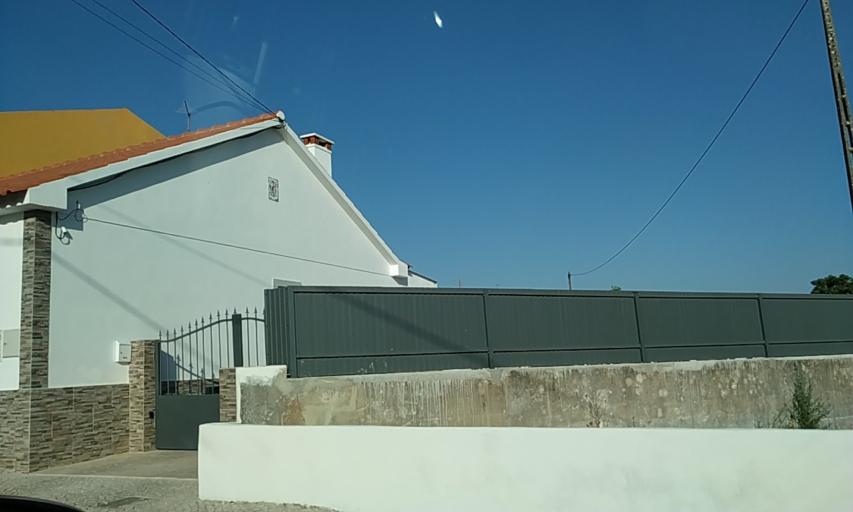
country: PT
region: Santarem
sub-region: Santarem
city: Santarem
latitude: 39.2543
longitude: -8.6823
